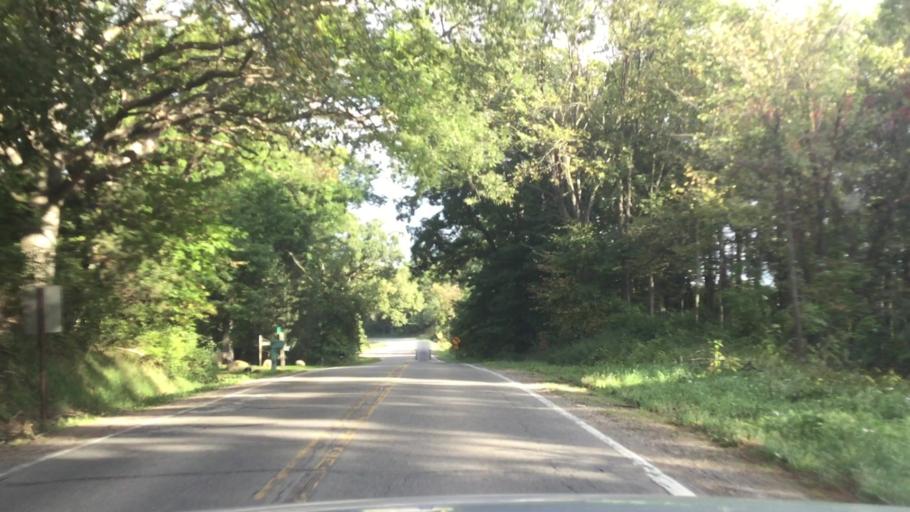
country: US
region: Michigan
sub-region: Livingston County
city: Brighton
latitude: 42.4875
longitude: -83.8522
